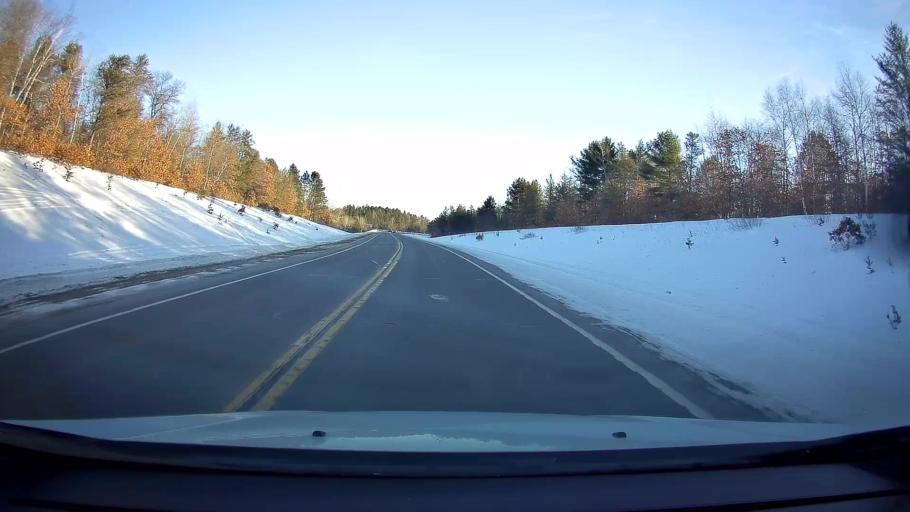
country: US
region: Wisconsin
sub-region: Washburn County
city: Spooner
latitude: 45.9068
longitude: -91.8103
